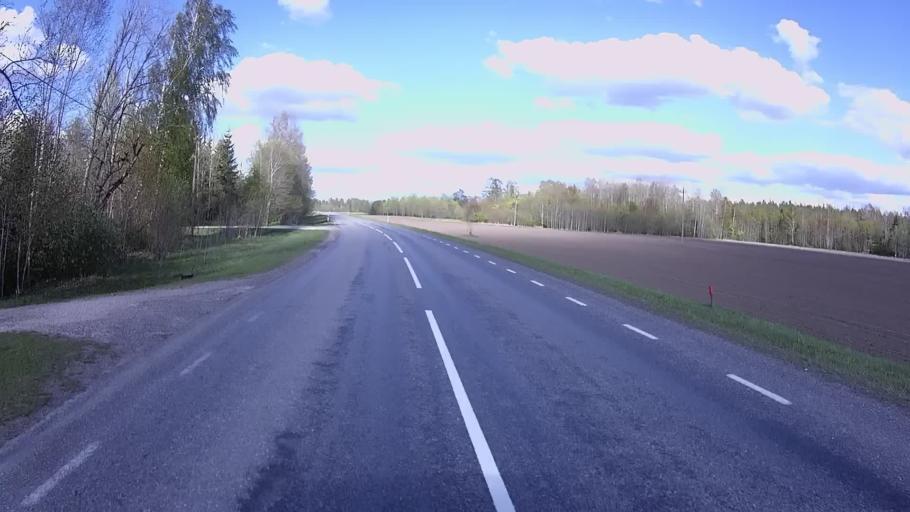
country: EE
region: Jogevamaa
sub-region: Poltsamaa linn
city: Poltsamaa
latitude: 58.7023
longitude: 26.1524
